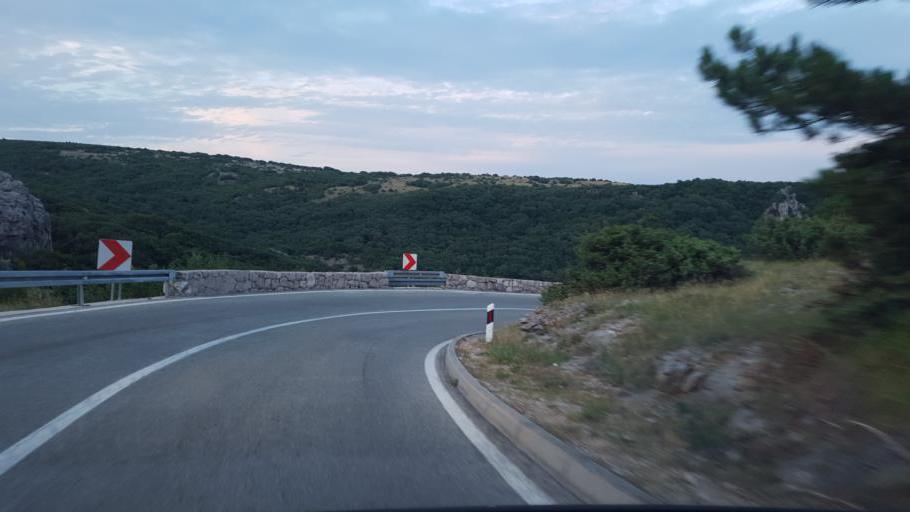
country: HR
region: Primorsko-Goranska
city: Punat
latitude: 45.0281
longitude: 14.6774
